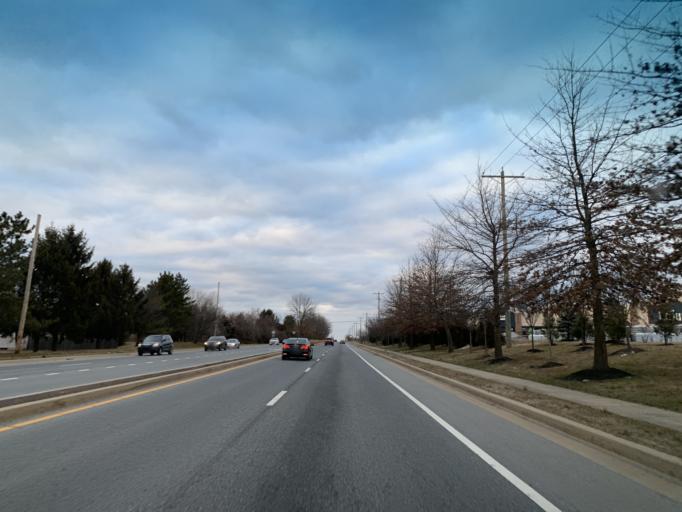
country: US
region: Delaware
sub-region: New Castle County
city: Bear
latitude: 39.6369
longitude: -75.6588
